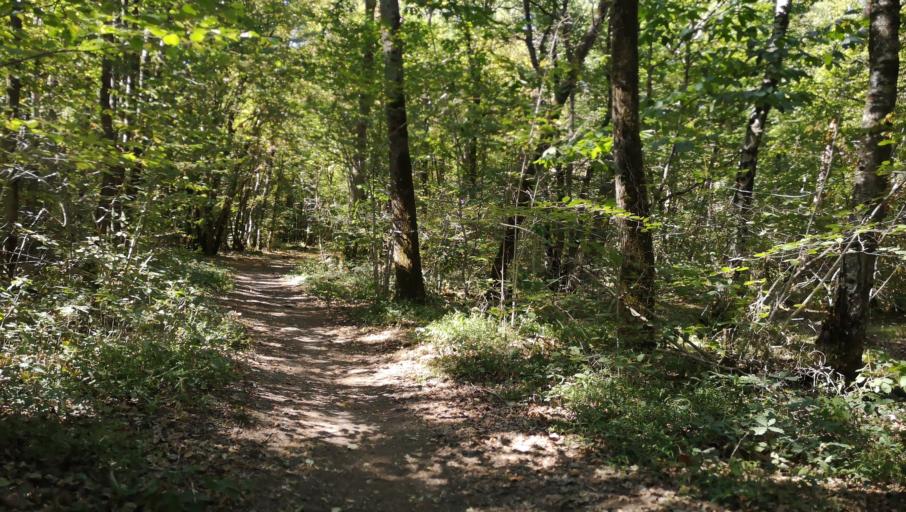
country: FR
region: Centre
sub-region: Departement du Loiret
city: Saran
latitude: 47.9591
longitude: 1.9013
